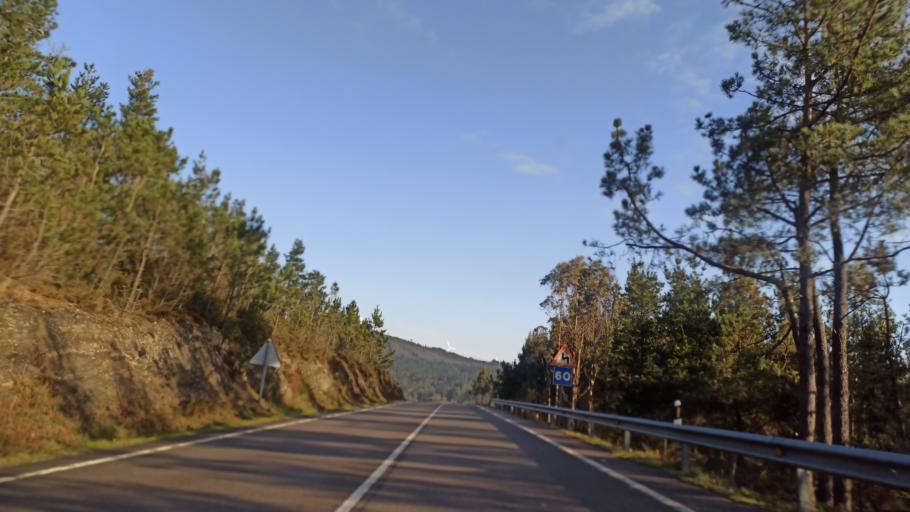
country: ES
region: Galicia
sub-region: Provincia da Coruna
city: As Pontes de Garcia Rodriguez
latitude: 43.4948
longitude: -7.8318
